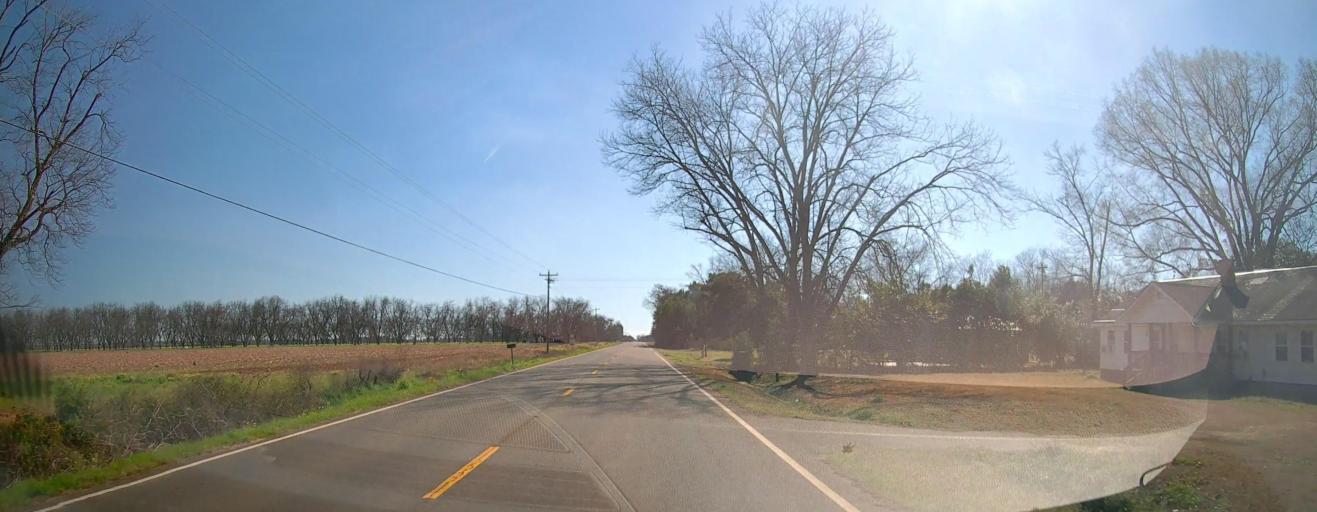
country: US
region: Georgia
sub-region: Macon County
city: Montezuma
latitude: 32.3388
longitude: -84.0204
